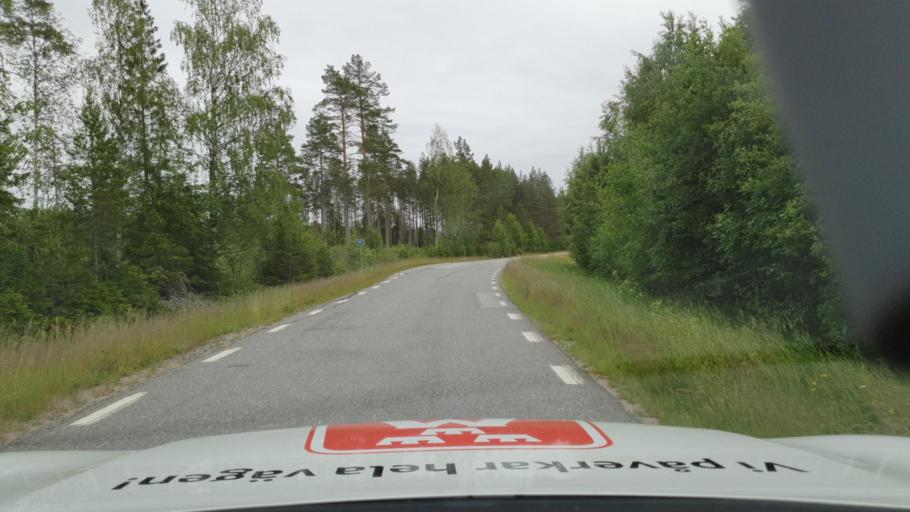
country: SE
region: Vaesterbotten
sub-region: Nordmalings Kommun
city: Nordmaling
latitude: 63.4964
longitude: 19.4330
